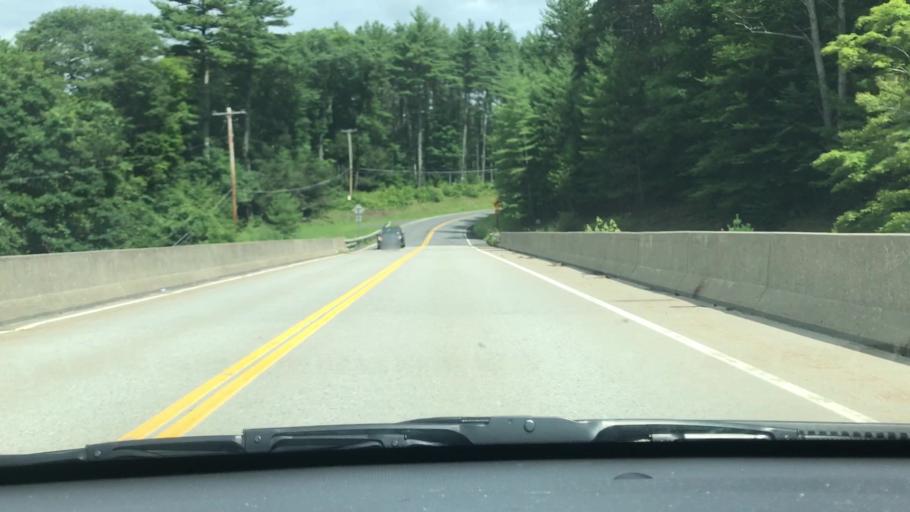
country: US
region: New York
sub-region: Ulster County
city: Shokan
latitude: 41.9924
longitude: -74.2779
